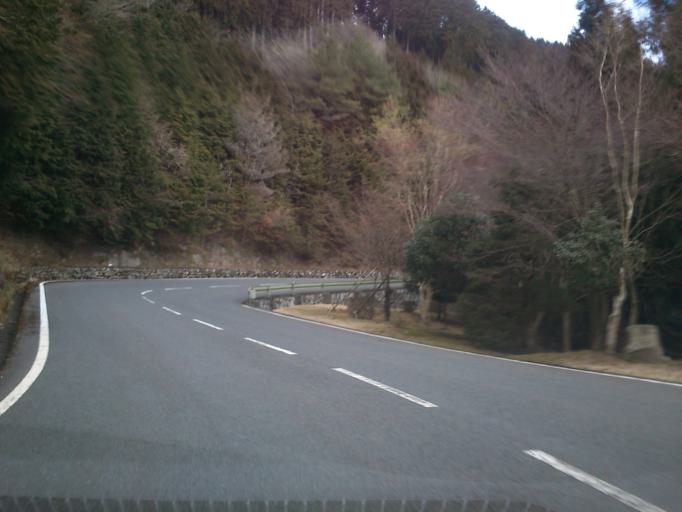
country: JP
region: Shiga Prefecture
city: Otsu-shi
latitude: 35.0613
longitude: 135.8362
